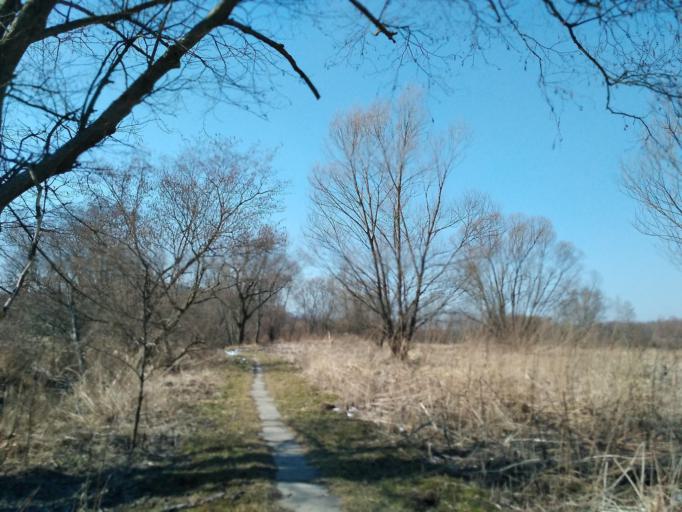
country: PL
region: Subcarpathian Voivodeship
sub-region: Powiat brzozowski
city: Domaradz
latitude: 49.7899
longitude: 21.9557
